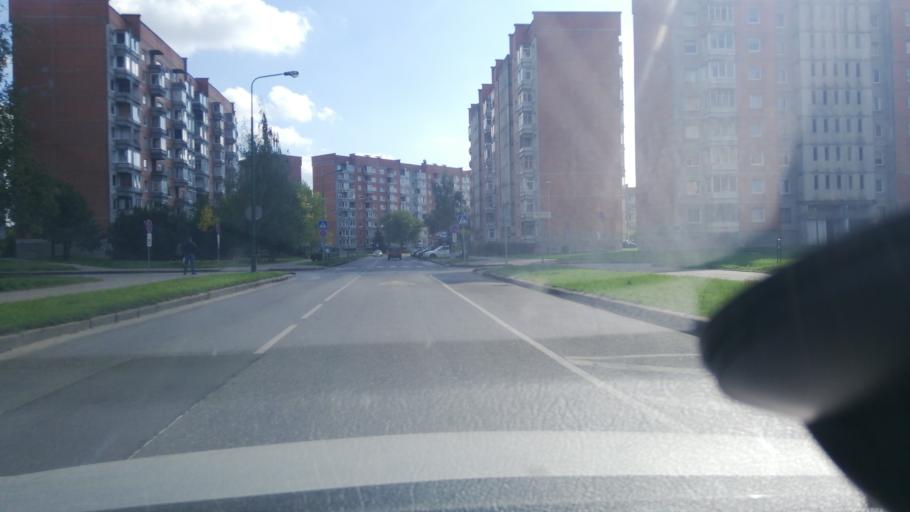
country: LT
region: Klaipedos apskritis
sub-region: Klaipeda
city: Klaipeda
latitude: 55.6686
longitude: 21.2008
